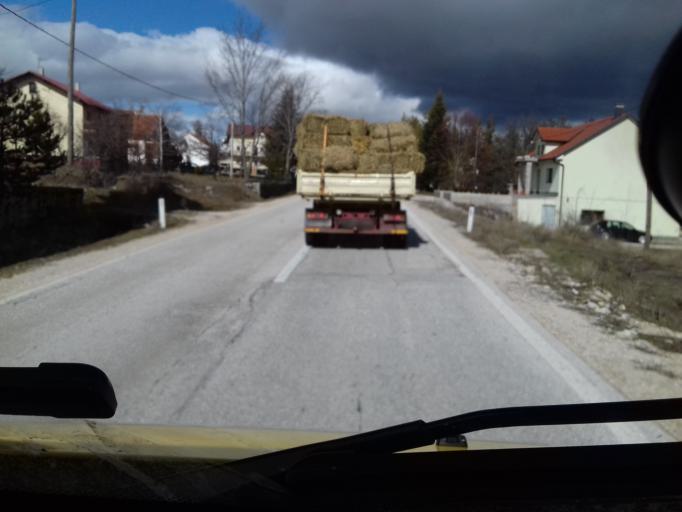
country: BA
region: Federation of Bosnia and Herzegovina
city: Dreznica
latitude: 43.6058
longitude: 17.2715
